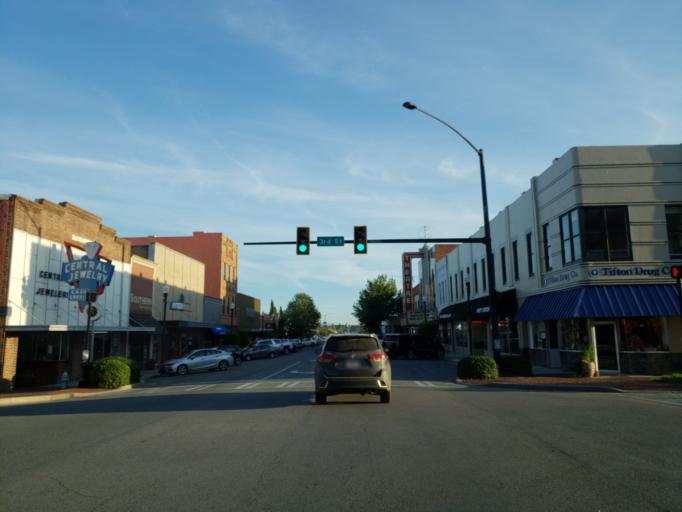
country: US
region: Georgia
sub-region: Tift County
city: Tifton
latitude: 31.4524
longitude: -83.5097
